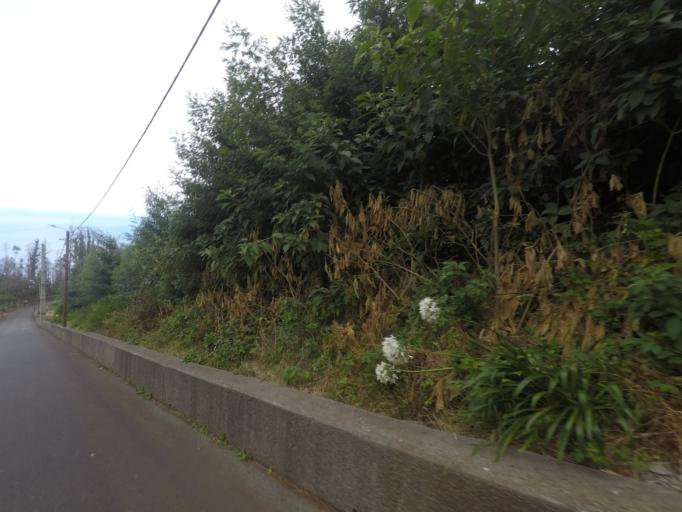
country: PT
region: Madeira
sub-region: Funchal
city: Nossa Senhora do Monte
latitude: 32.6697
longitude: -16.8832
